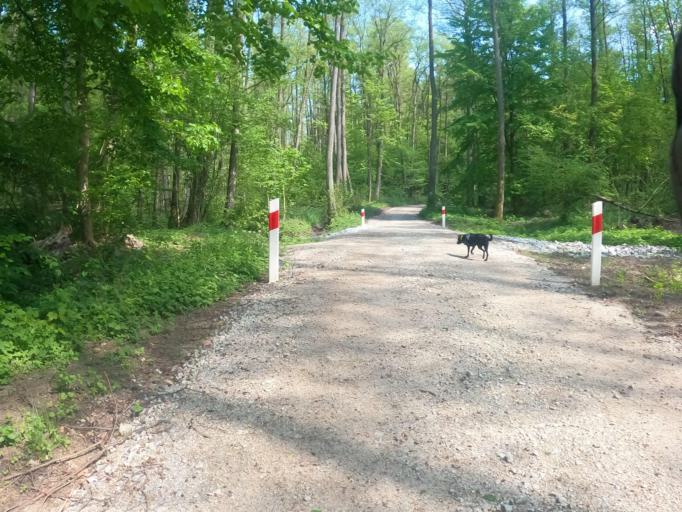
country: PL
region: West Pomeranian Voivodeship
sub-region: Powiat mysliborski
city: Barlinek
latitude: 53.0159
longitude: 15.2437
